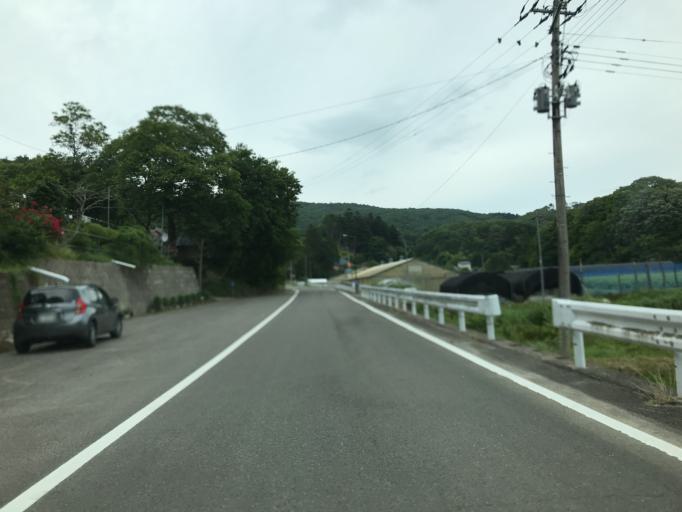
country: JP
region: Fukushima
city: Funehikimachi-funehiki
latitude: 37.4179
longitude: 140.7076
